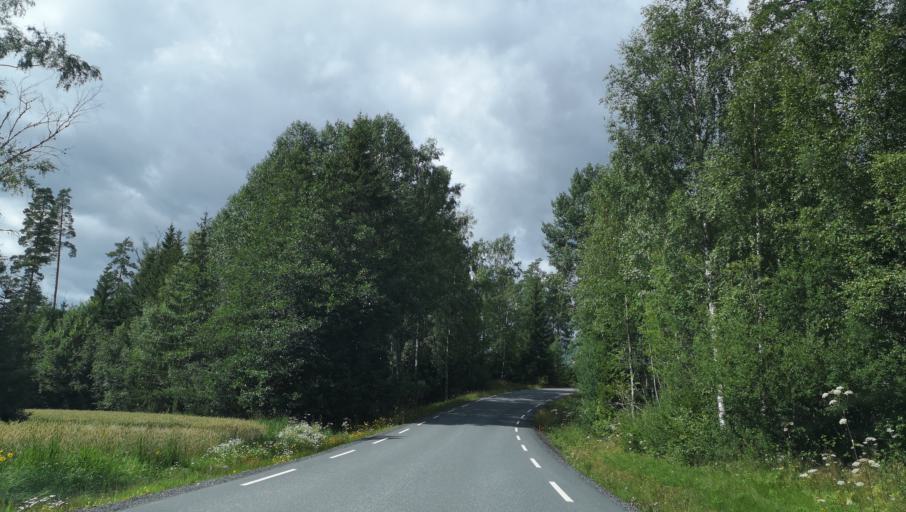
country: NO
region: Ostfold
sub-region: Hobol
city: Tomter
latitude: 59.6734
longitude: 10.9694
